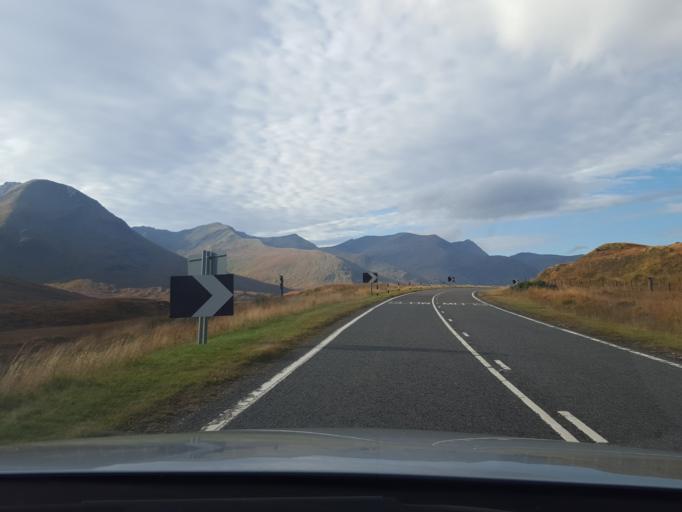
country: GB
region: Scotland
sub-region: Highland
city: Fort William
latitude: 57.1561
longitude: -5.1744
